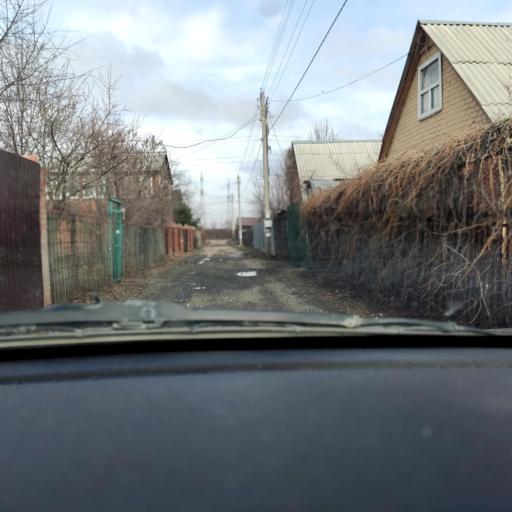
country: RU
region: Samara
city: Tol'yatti
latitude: 53.5872
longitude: 49.2909
